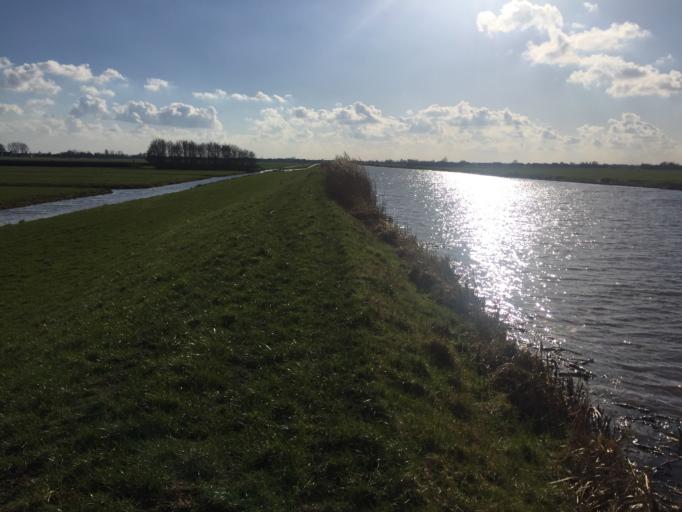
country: NL
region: South Holland
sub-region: Bodegraven-Reeuwijk
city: Bodegraven
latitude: 52.0619
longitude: 4.8047
